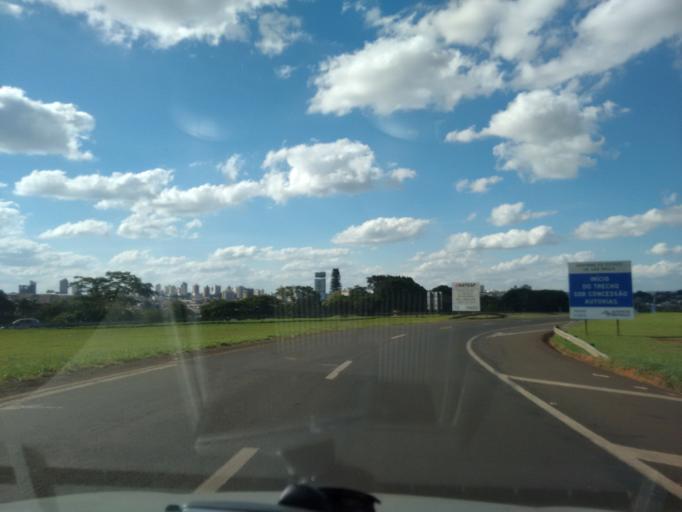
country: BR
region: Sao Paulo
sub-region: Araraquara
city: Araraquara
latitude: -21.8177
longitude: -48.1772
